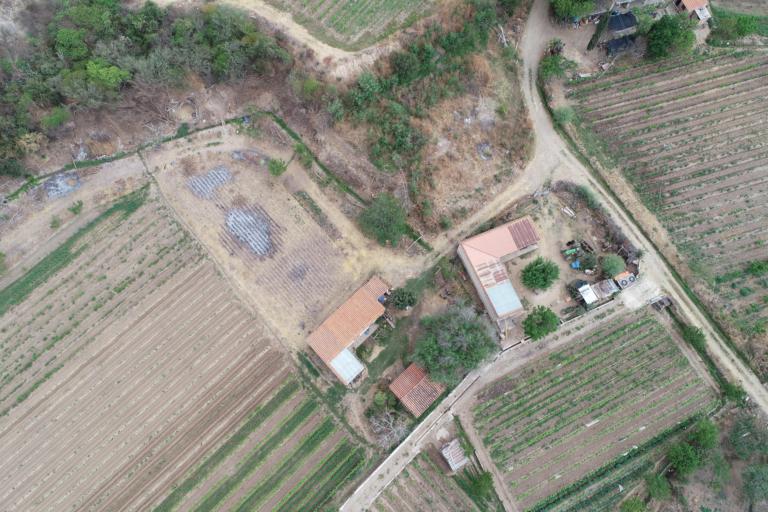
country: BO
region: Tarija
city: Tarija
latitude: -21.5997
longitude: -64.6175
